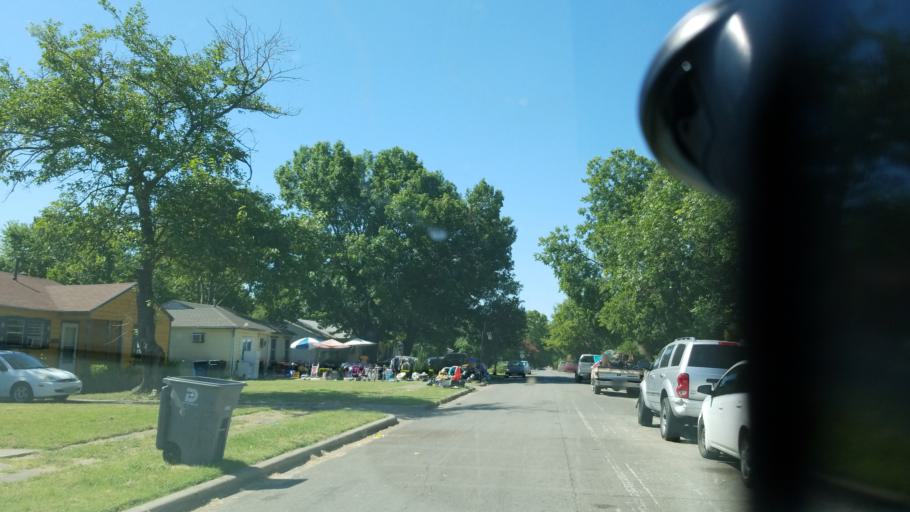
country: US
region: Texas
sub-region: Dallas County
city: Dallas
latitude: 32.7058
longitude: -96.8122
